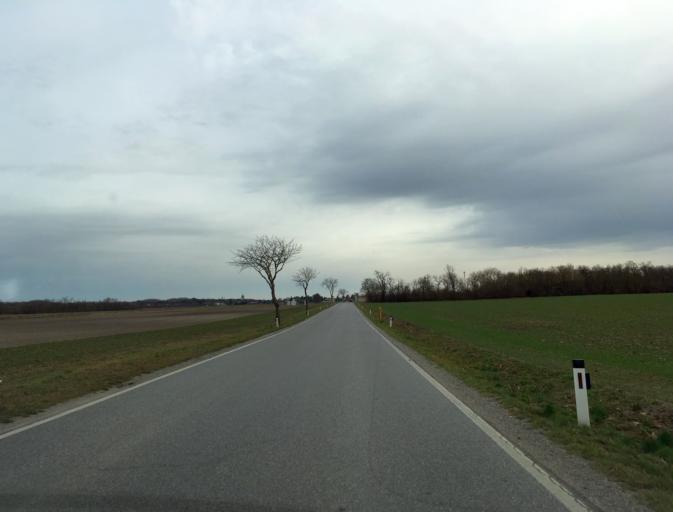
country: AT
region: Lower Austria
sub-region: Politischer Bezirk Ganserndorf
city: Leopoldsdorf im Marchfelde
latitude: 48.2349
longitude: 16.6747
